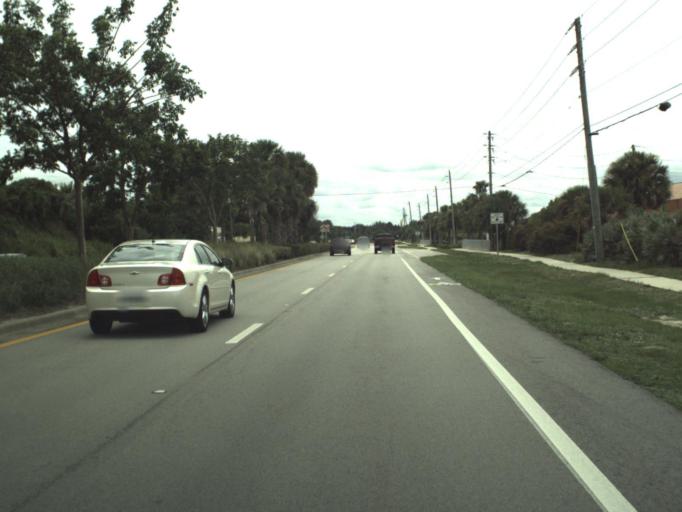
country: US
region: Florida
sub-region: Palm Beach County
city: Juno Beach
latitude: 26.8713
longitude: -80.0552
